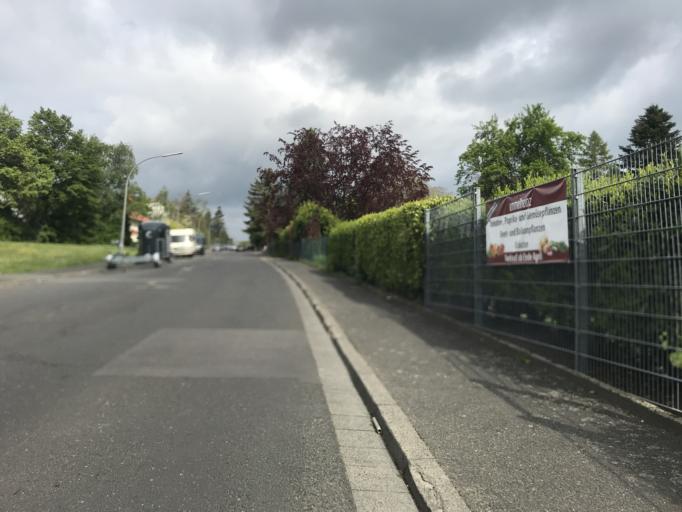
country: DE
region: Hesse
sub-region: Regierungsbezirk Darmstadt
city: Walluf
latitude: 50.0592
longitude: 8.1908
